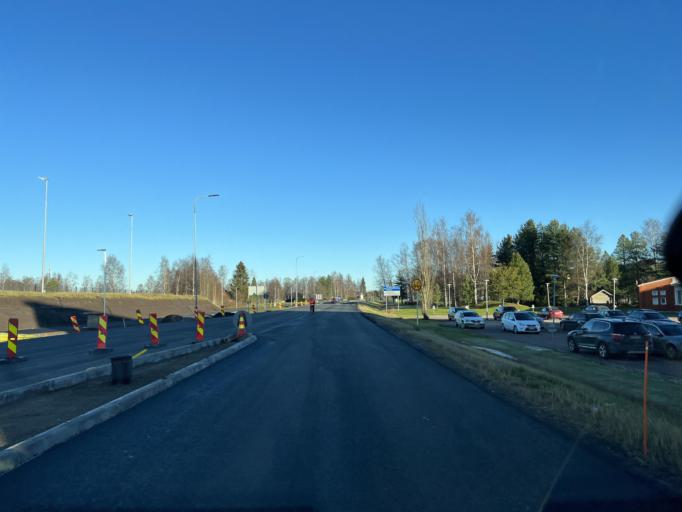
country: FI
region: Northern Ostrobothnia
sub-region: Ylivieska
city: Ylivieska
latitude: 64.0750
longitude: 24.5149
